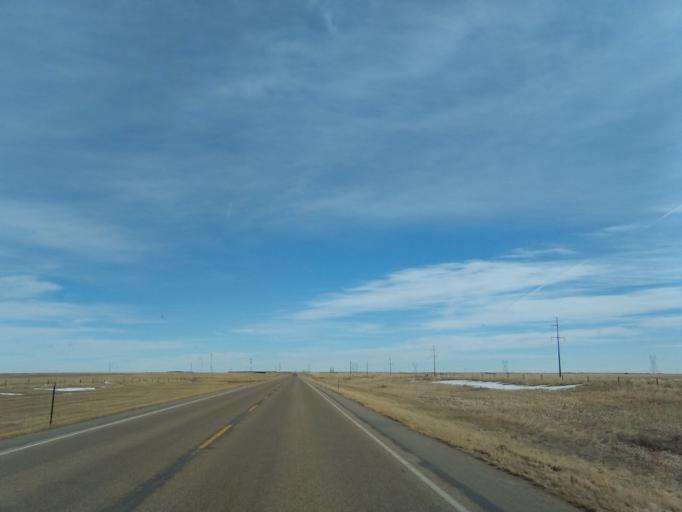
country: US
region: Wyoming
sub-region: Laramie County
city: Pine Bluffs
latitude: 41.4327
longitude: -104.3689
